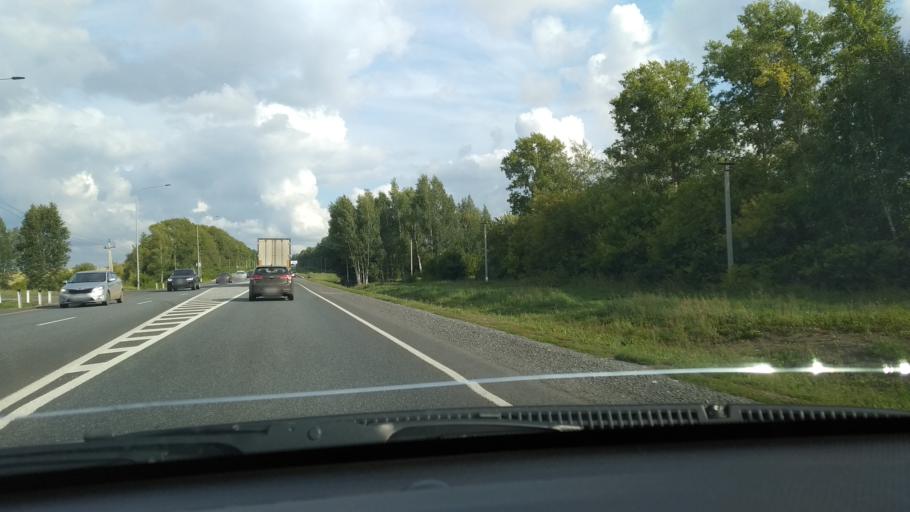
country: RU
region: Tatarstan
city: Stolbishchi
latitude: 55.6528
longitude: 49.3196
